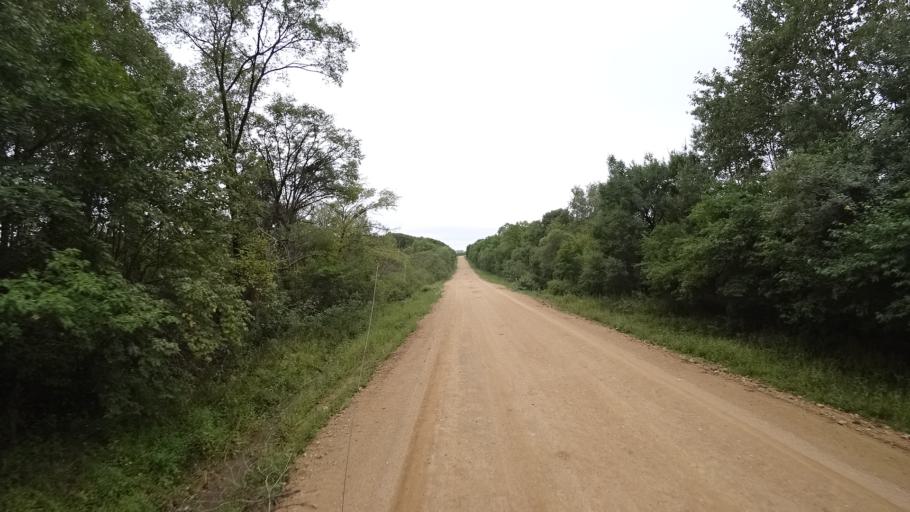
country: RU
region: Primorskiy
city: Monastyrishche
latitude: 44.0857
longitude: 132.5962
